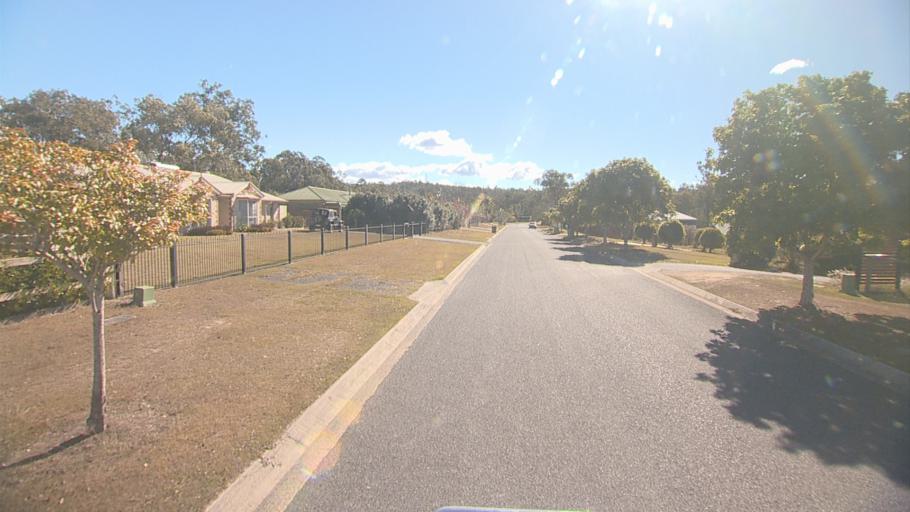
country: AU
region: Queensland
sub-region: Ipswich
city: Springfield Lakes
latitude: -27.7272
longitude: 152.9186
